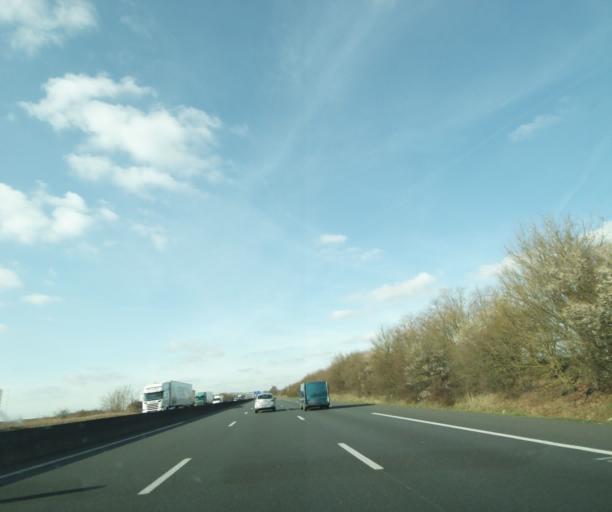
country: FR
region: Centre
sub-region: Departement d'Eure-et-Loir
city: Janville
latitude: 48.1923
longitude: 1.8528
